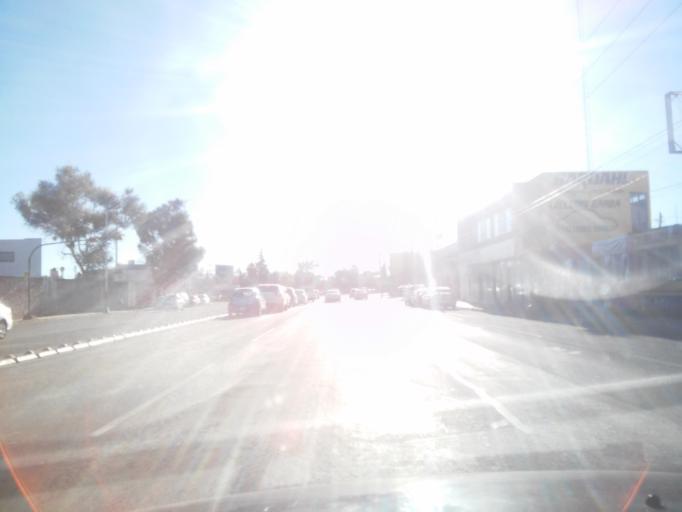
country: MX
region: Durango
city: Victoria de Durango
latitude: 24.0281
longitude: -104.6448
